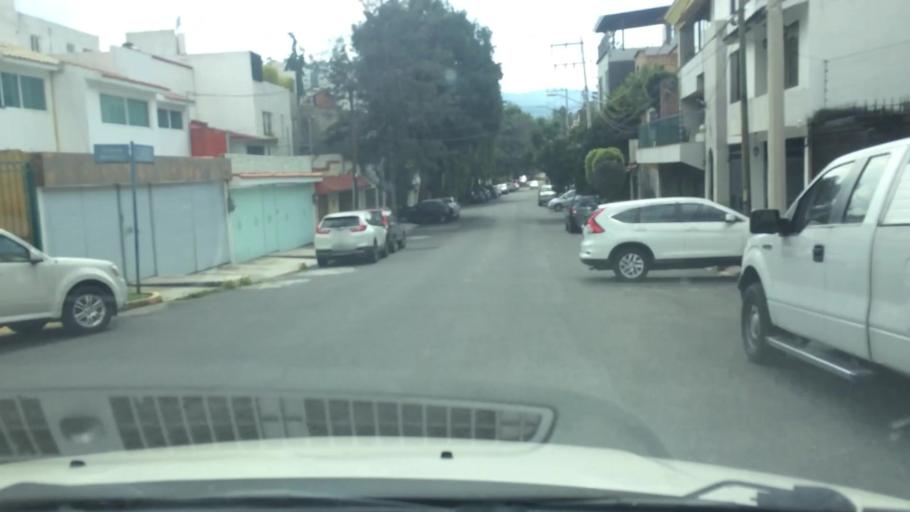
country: MX
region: Mexico City
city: Magdalena Contreras
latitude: 19.3418
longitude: -99.2433
